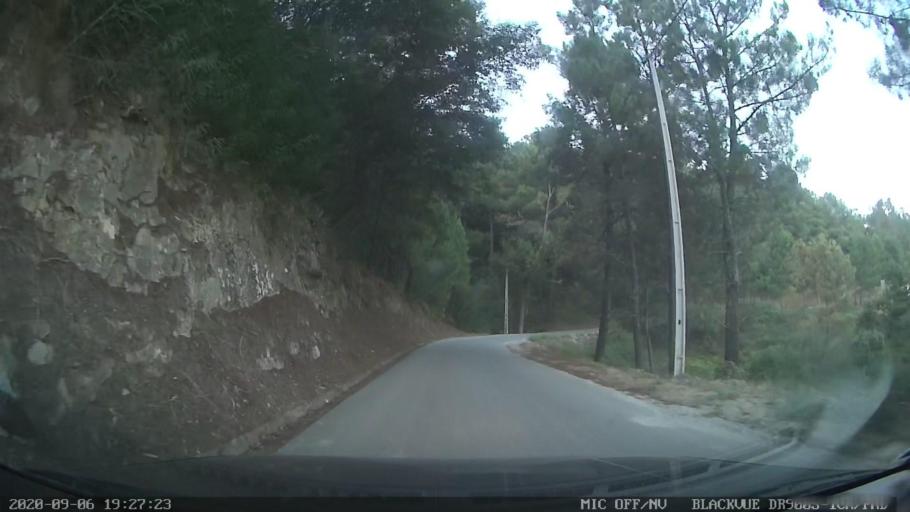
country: PT
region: Vila Real
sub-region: Mesao Frio
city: Mesao Frio
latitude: 41.1812
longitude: -7.9106
